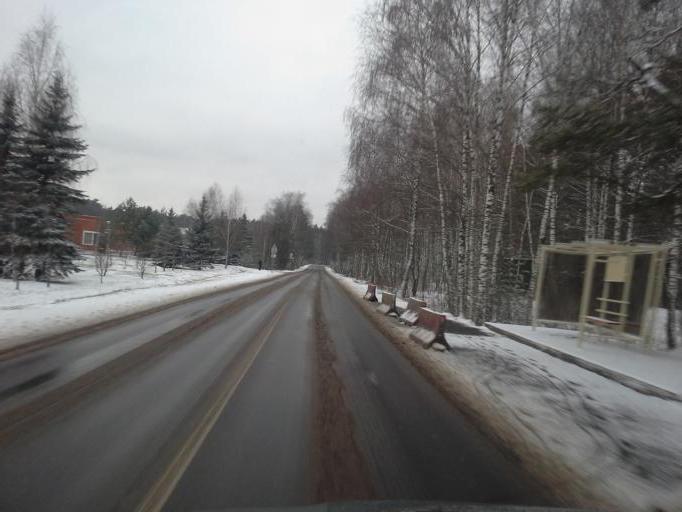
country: RU
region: Moskovskaya
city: Nikolina Gora
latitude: 55.7423
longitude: 37.0798
